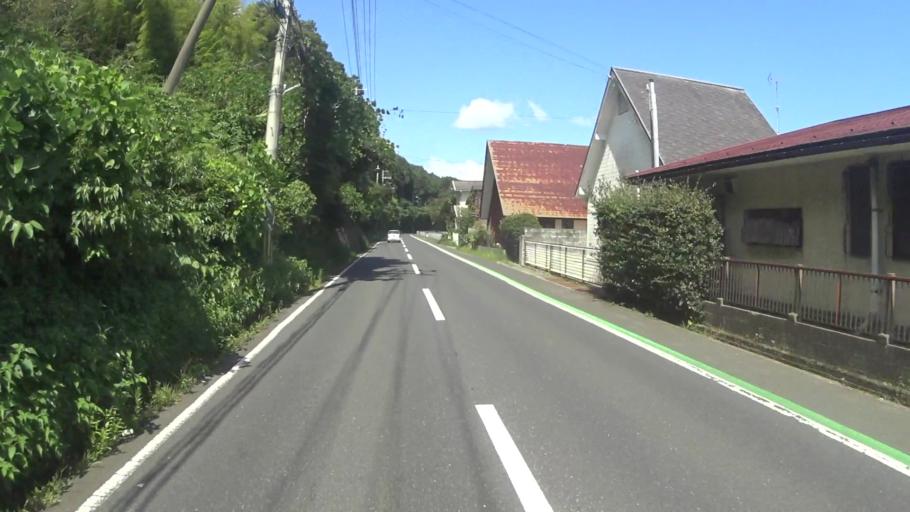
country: JP
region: Kyoto
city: Miyazu
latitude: 35.5956
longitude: 135.2131
